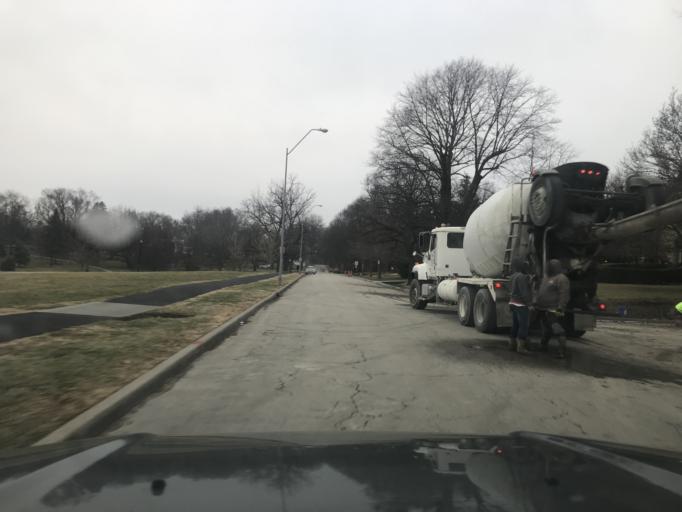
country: US
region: Kansas
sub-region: Johnson County
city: Westwood
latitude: 39.0302
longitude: -94.5971
